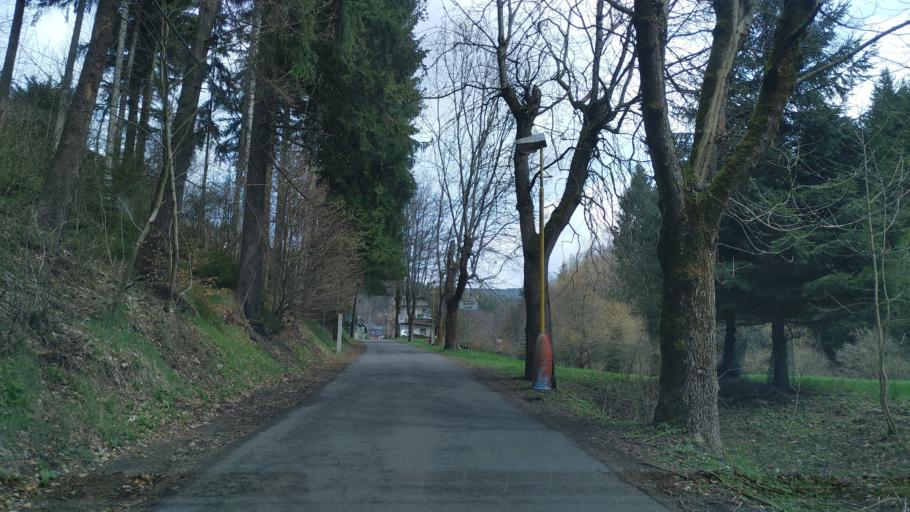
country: CZ
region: Karlovarsky
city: Jachymov
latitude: 50.3641
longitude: 12.9470
